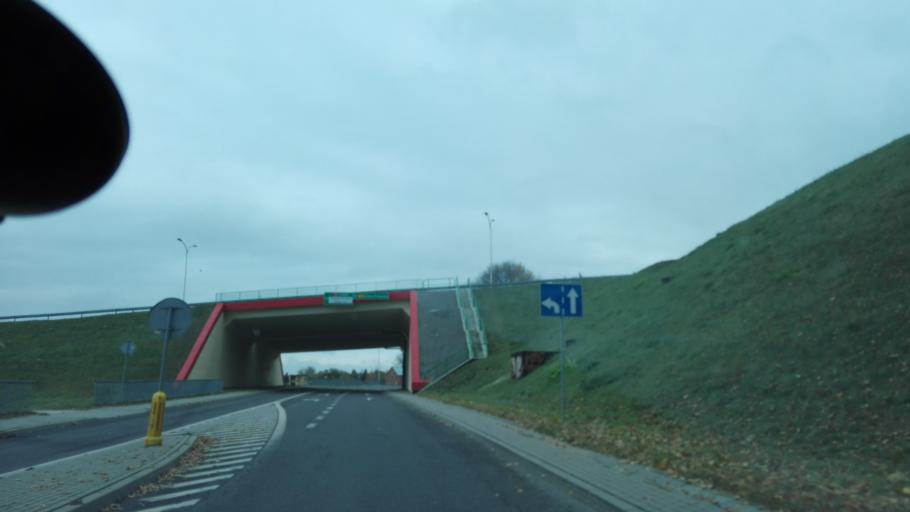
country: PL
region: Lublin Voivodeship
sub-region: Powiat pulawski
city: Pulawy
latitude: 51.4377
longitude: 21.9114
